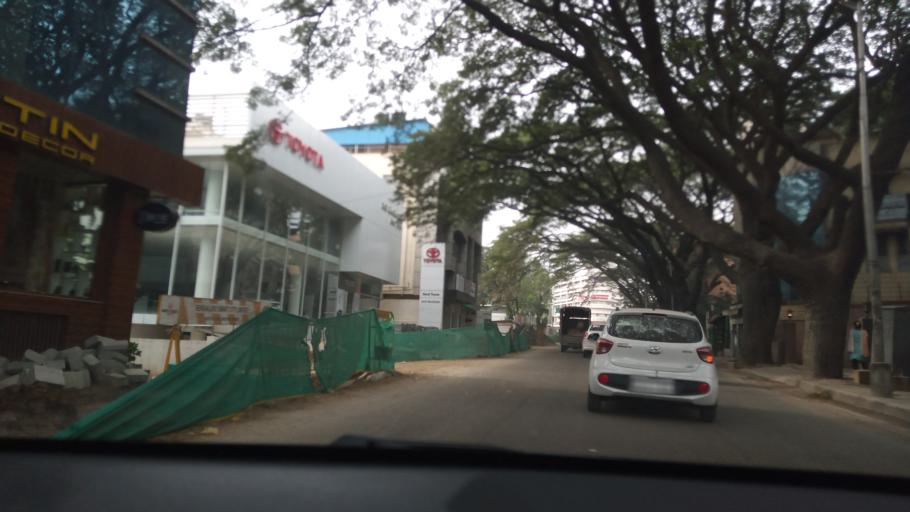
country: IN
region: Karnataka
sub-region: Bangalore Urban
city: Bangalore
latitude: 12.9860
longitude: 77.5978
